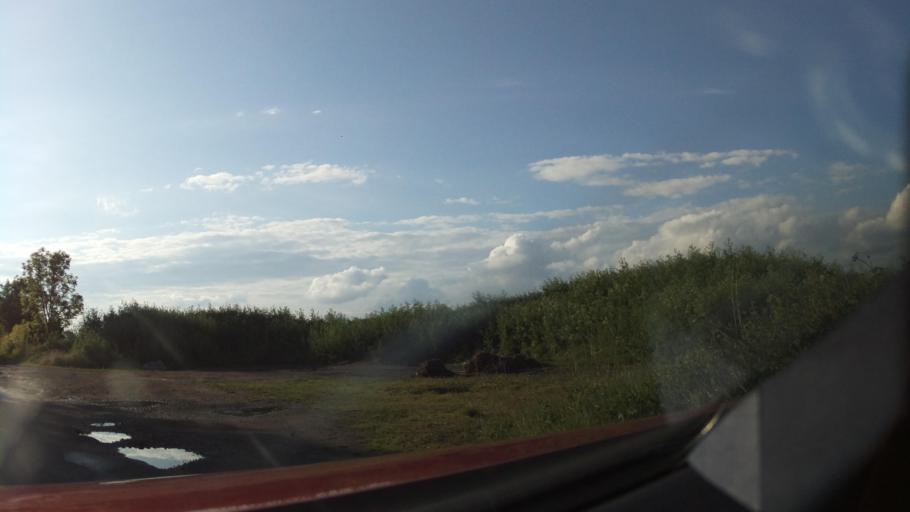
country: GB
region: England
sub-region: Lincolnshire
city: Navenby
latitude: 53.1154
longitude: -0.6193
